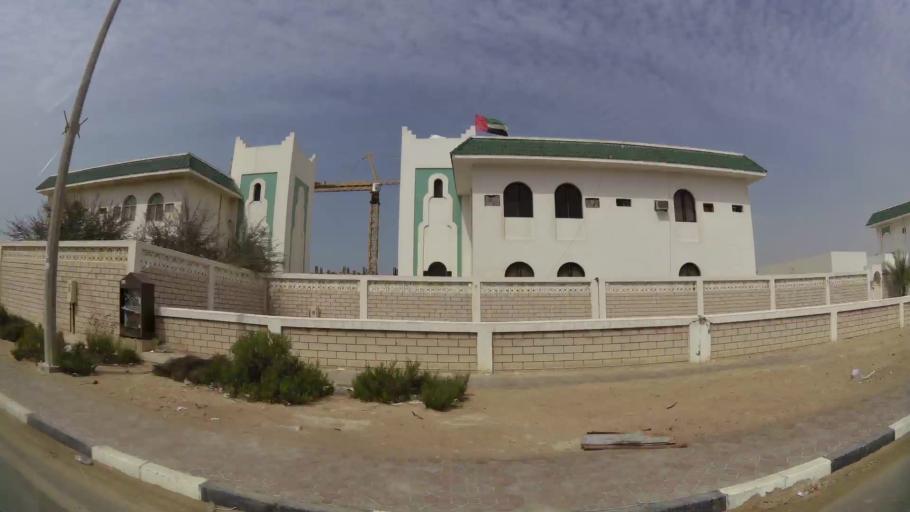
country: AE
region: Abu Dhabi
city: Abu Dhabi
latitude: 24.5328
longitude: 54.6856
